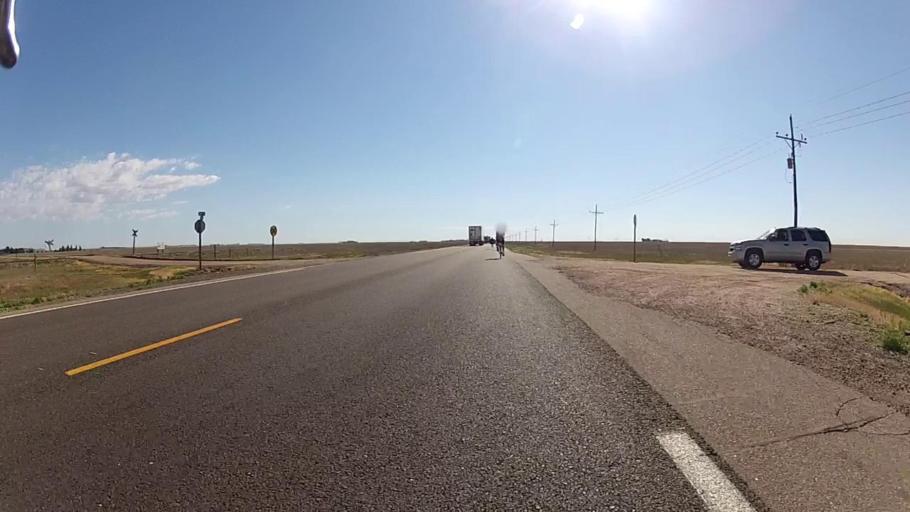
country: US
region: Kansas
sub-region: Gray County
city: Cimarron
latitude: 37.5812
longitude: -100.5070
